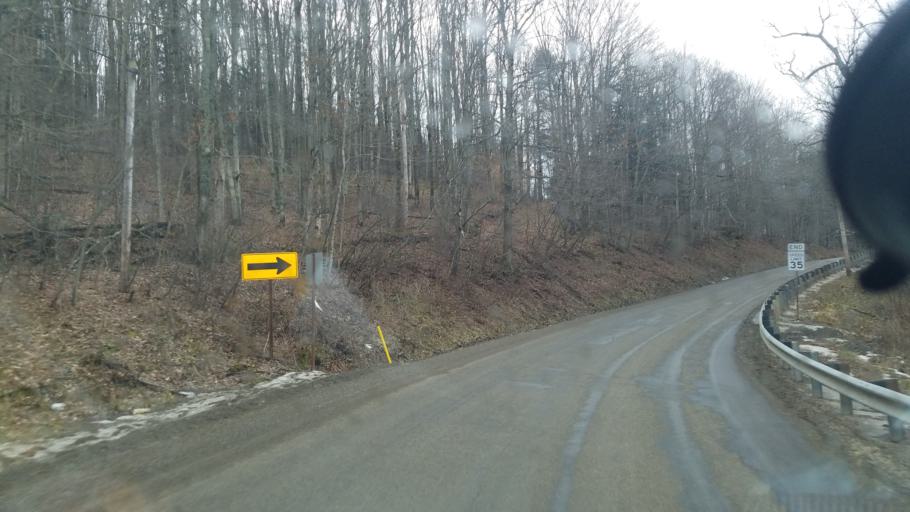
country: US
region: New York
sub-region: Allegany County
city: Andover
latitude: 41.9452
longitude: -77.8217
